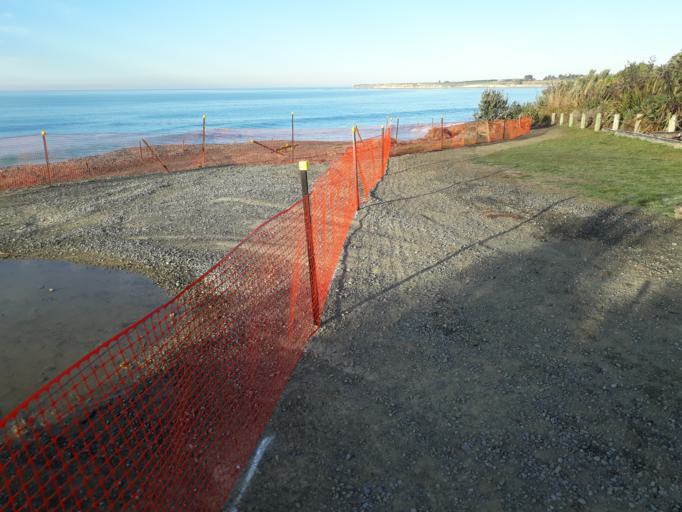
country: NZ
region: Canterbury
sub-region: Timaru District
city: Timaru
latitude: -44.4151
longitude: 171.2641
